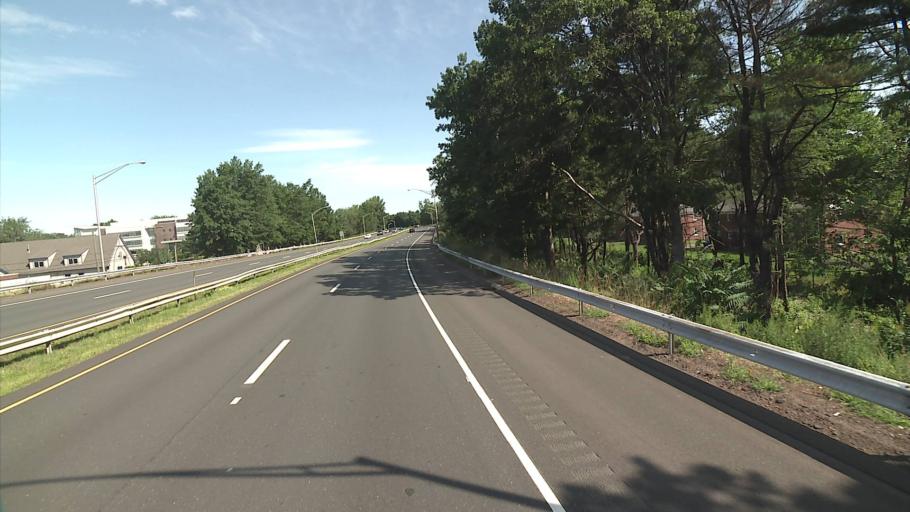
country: US
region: Connecticut
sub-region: Hartford County
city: Wethersfield
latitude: 41.7473
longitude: -72.6417
